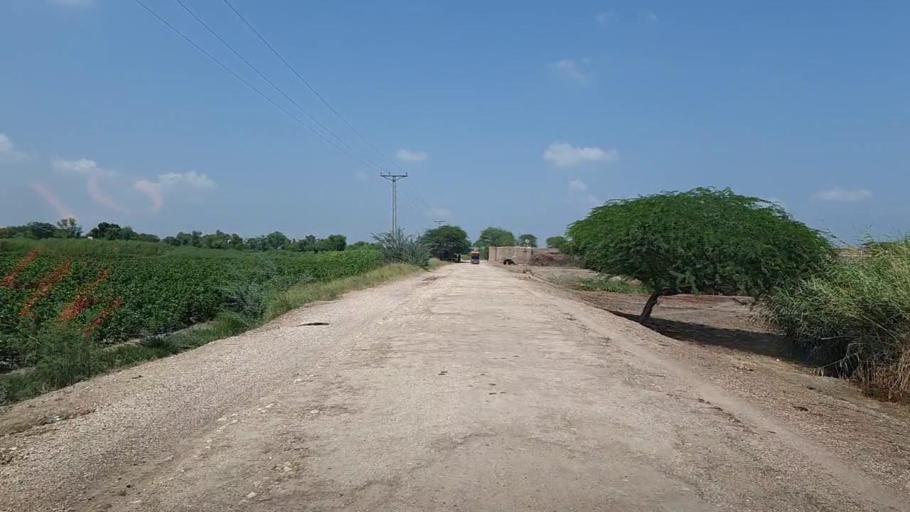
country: PK
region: Sindh
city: Kandiaro
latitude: 26.9864
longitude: 68.2458
